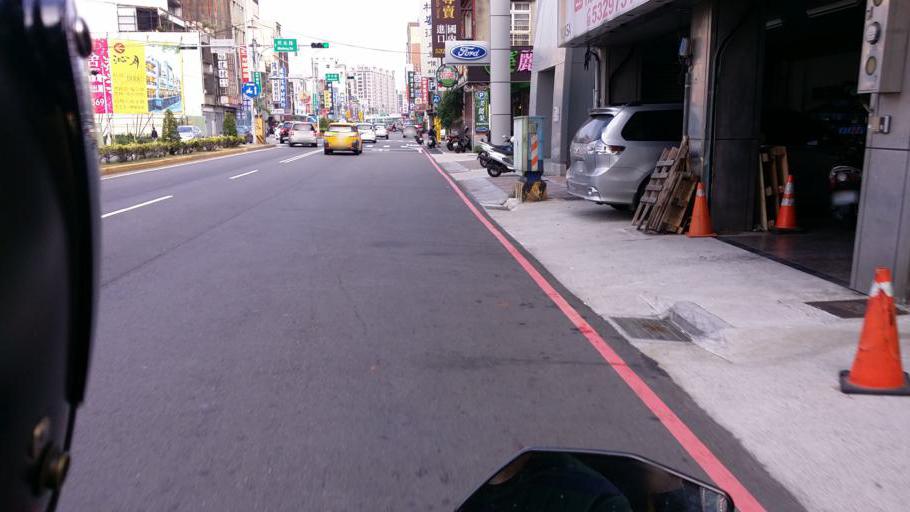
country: TW
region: Taiwan
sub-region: Hsinchu
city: Hsinchu
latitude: 24.8066
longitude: 120.9790
